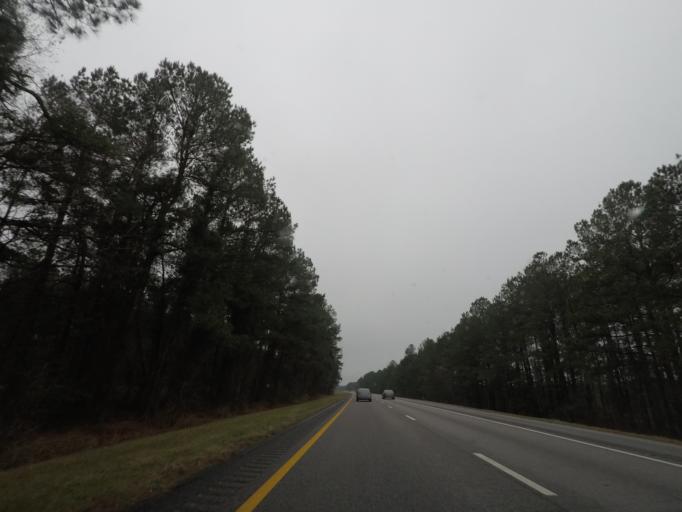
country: US
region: South Carolina
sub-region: Sumter County
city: East Sumter
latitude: 33.9104
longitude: -80.0879
